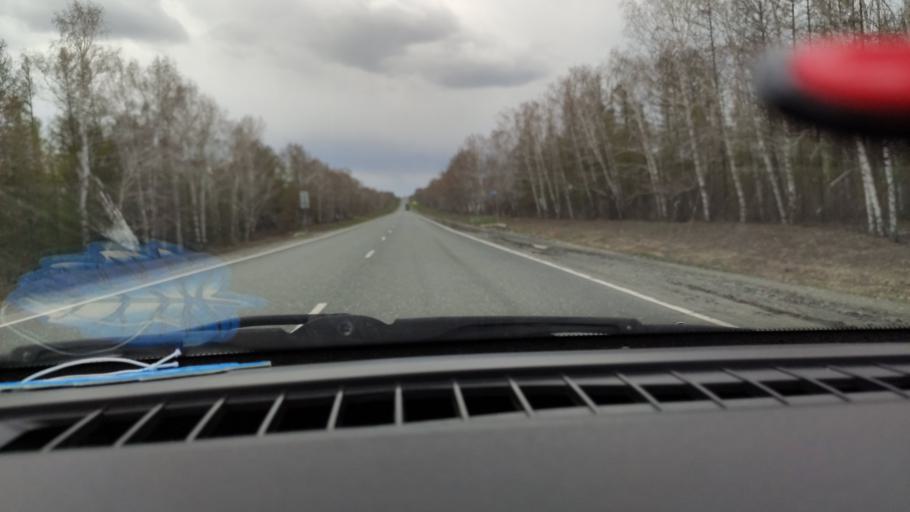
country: RU
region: Saratov
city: Sennoy
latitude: 52.1230
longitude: 46.8490
